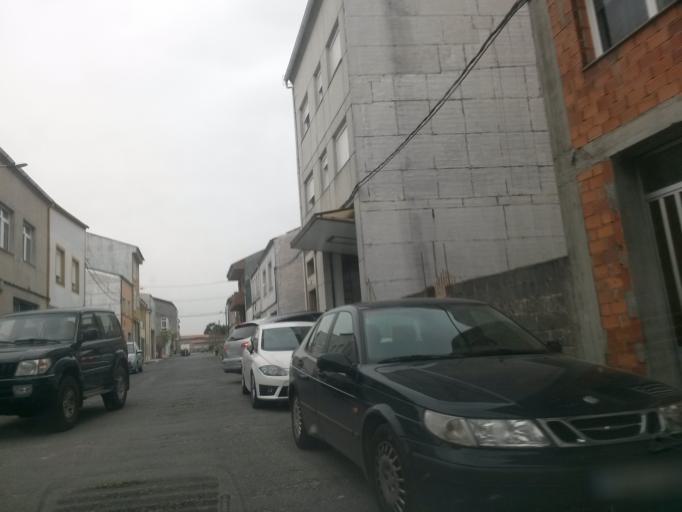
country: ES
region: Galicia
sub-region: Provincia de Lugo
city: Lugo
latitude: 43.0246
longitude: -7.5540
